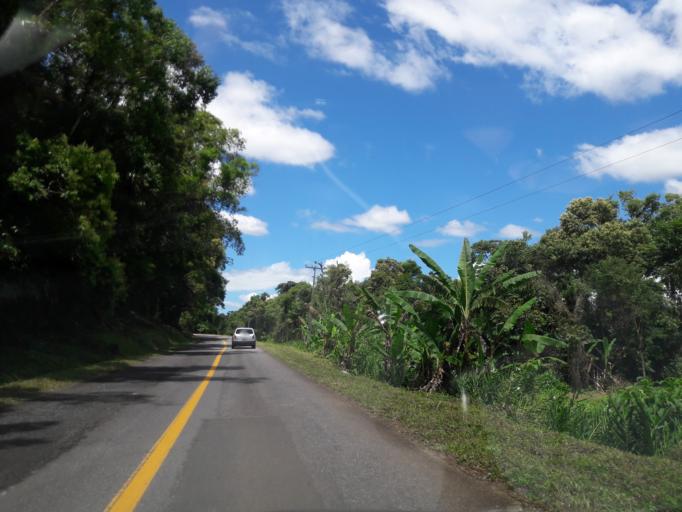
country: BR
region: Parana
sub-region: Antonina
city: Antonina
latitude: -25.4192
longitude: -48.8257
